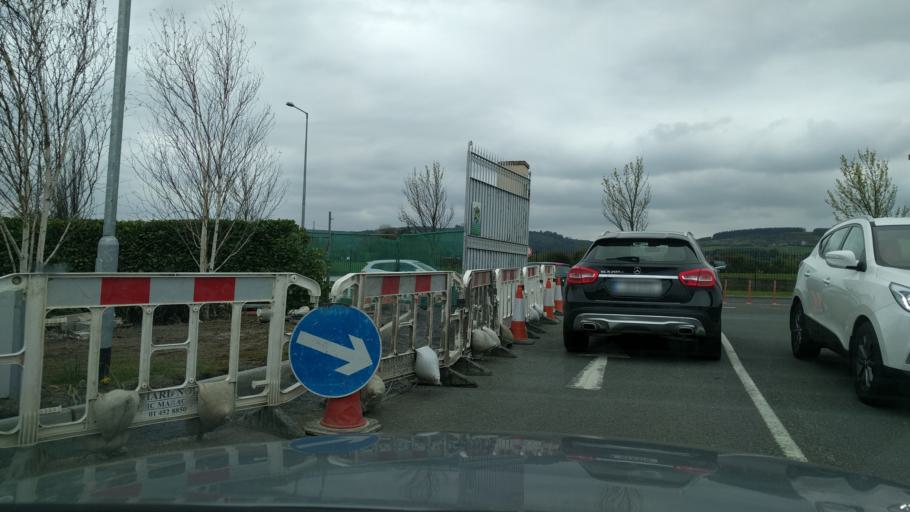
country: IE
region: Leinster
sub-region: South Dublin
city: Saggart
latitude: 53.2837
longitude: -6.4569
